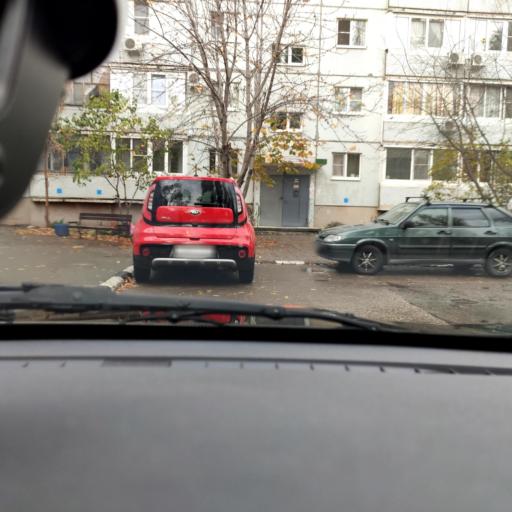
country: RU
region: Samara
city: Tol'yatti
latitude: 53.5194
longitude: 49.2968
